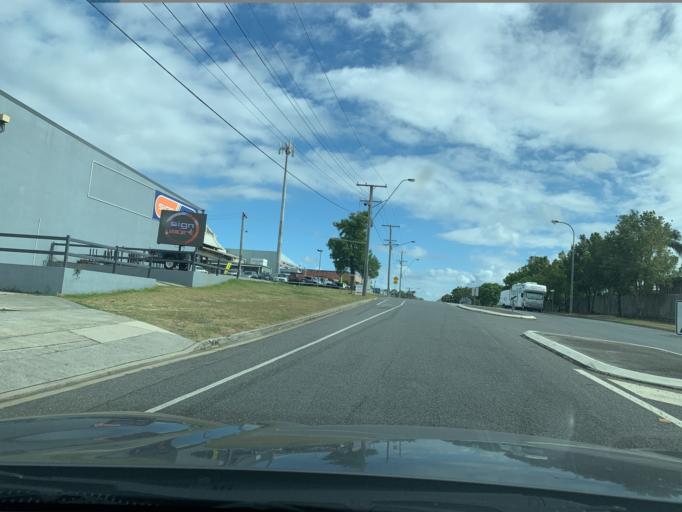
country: AU
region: Queensland
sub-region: Brisbane
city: Wynnum West
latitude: -27.4778
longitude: 153.1404
